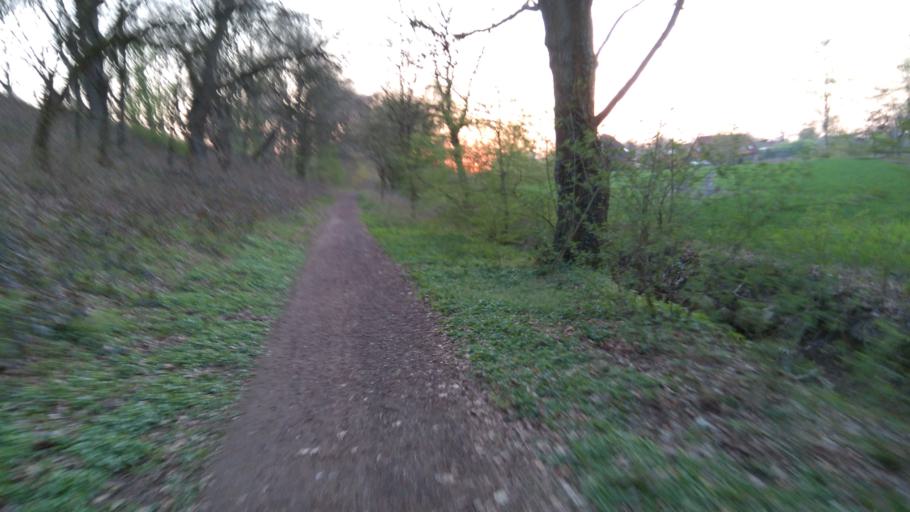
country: DE
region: Lower Saxony
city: Bargstedt
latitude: 53.4565
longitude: 9.4578
